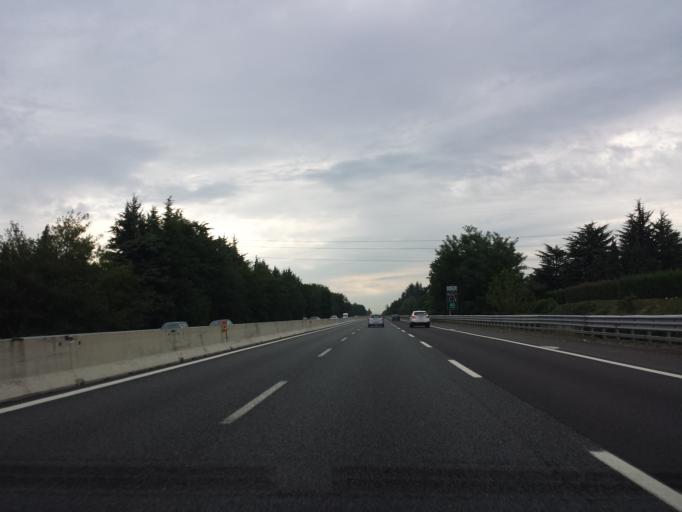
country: IT
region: Lombardy
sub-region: Provincia di Varese
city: Olgiate Olona
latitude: 45.6356
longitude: 8.8677
